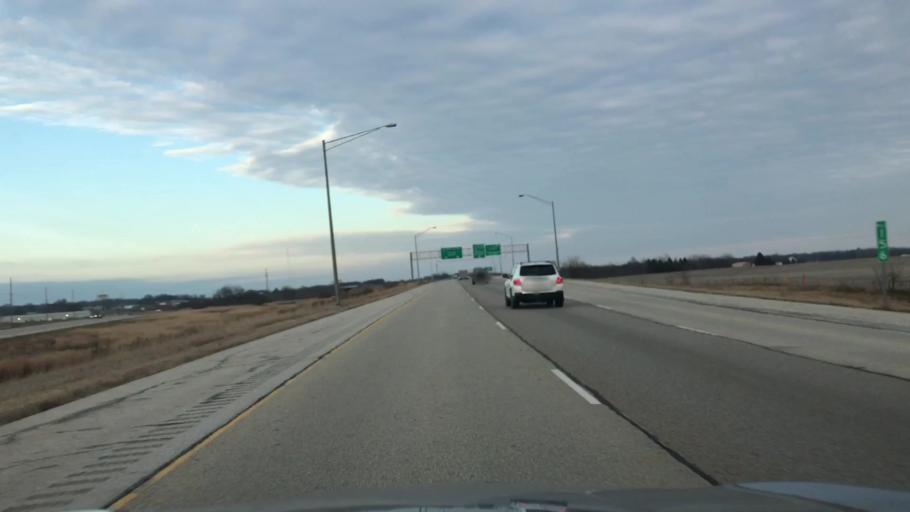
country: US
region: Illinois
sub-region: McLean County
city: Bloomington
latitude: 40.4308
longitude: -89.0336
